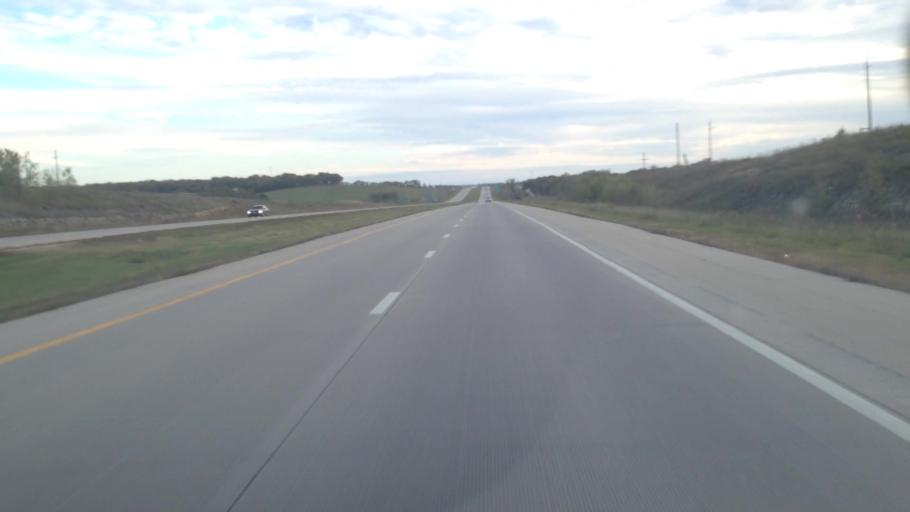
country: US
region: Kansas
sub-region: Douglas County
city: Baldwin City
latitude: 38.8059
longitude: -95.2692
